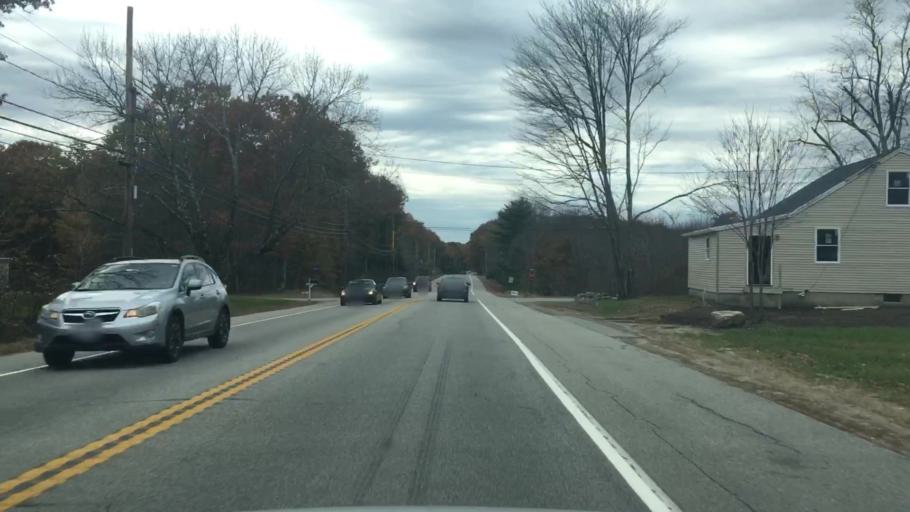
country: US
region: Maine
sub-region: York County
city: Alfred
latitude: 43.4763
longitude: -70.6617
